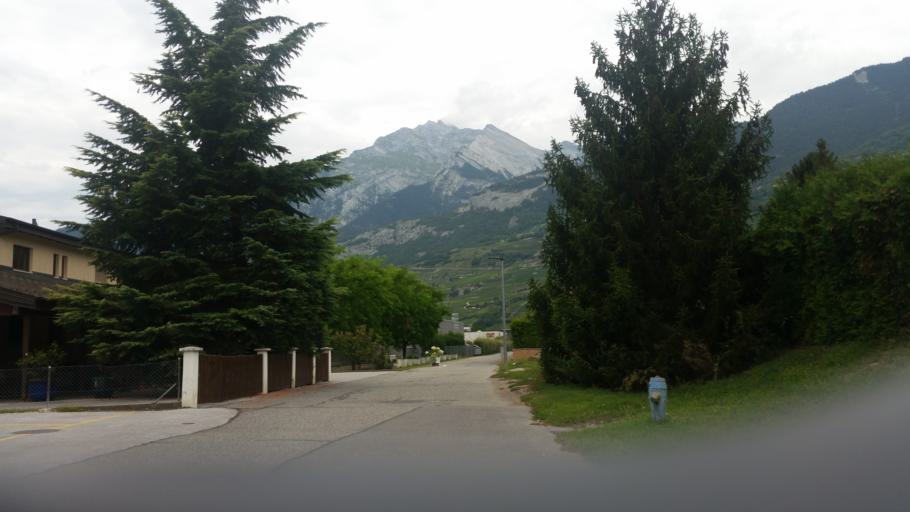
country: CH
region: Valais
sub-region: Conthey District
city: Conthey
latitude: 46.2252
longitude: 7.2993
